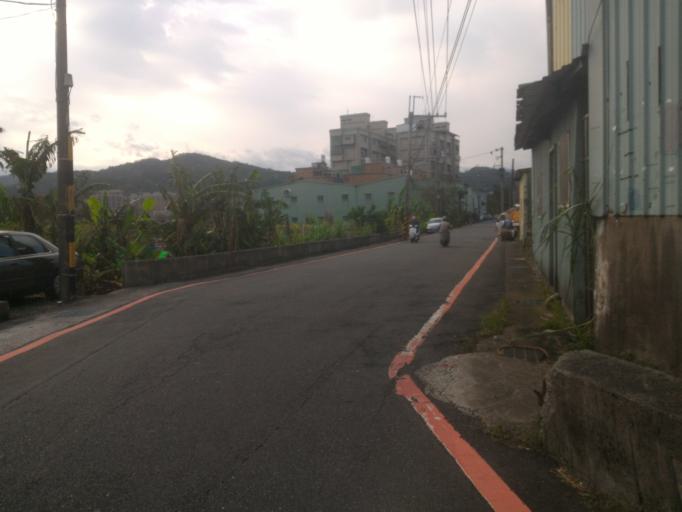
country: TW
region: Taipei
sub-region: Taipei
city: Banqiao
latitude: 24.9581
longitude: 121.4046
